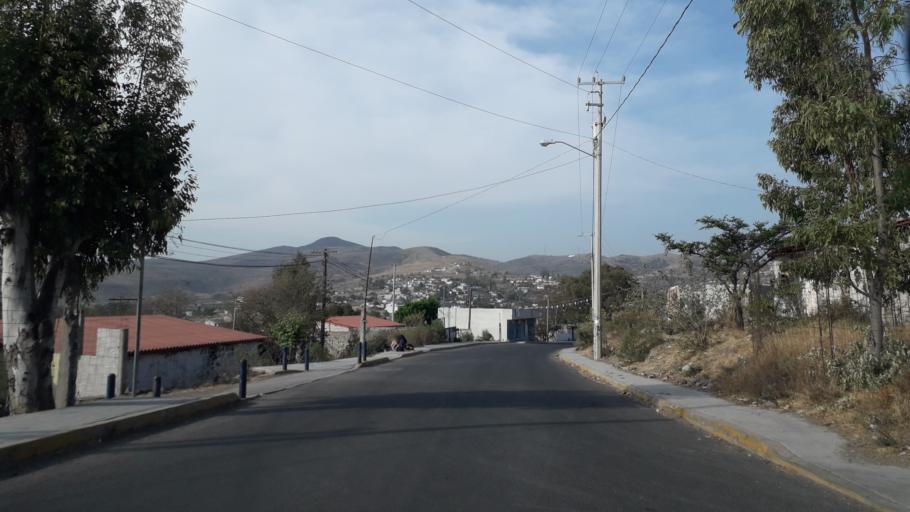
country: MX
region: Puebla
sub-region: Puebla
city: San Andres Azumiatla
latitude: 18.9079
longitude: -98.2432
